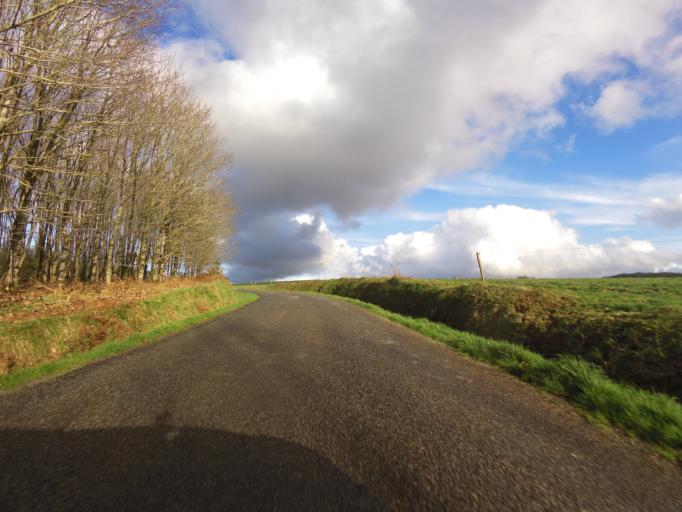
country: FR
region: Brittany
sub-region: Departement des Cotes-d'Armor
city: Plouguernevel
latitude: 48.1854
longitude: -3.2506
